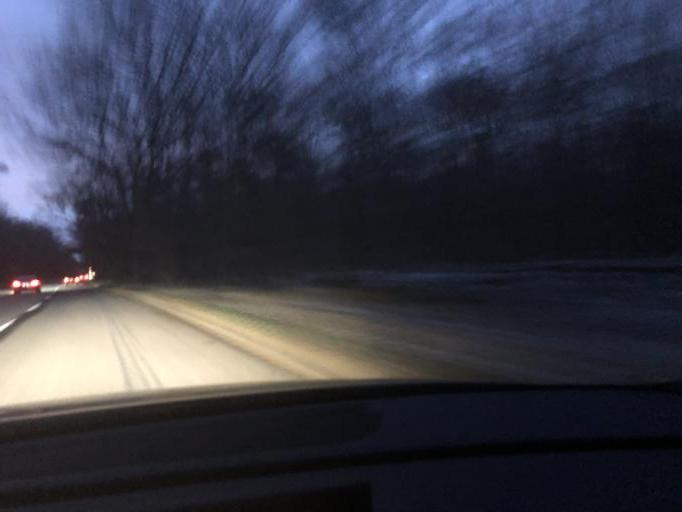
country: US
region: New Jersey
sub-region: Essex County
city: Northfield
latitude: 40.7663
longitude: -74.3397
